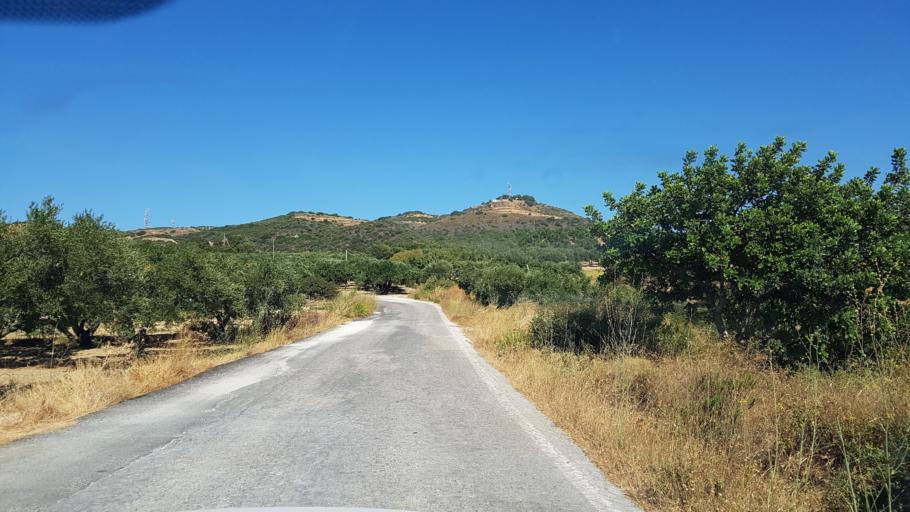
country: GR
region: Crete
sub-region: Nomos Chanias
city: Kolympari
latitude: 35.5010
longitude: 23.7255
